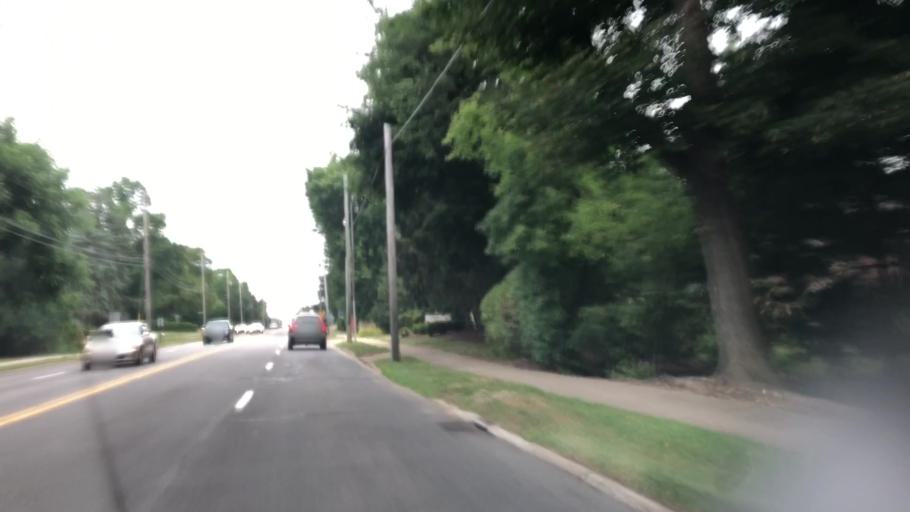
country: US
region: Ohio
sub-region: Stark County
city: North Canton
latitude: 40.8546
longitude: -81.3942
